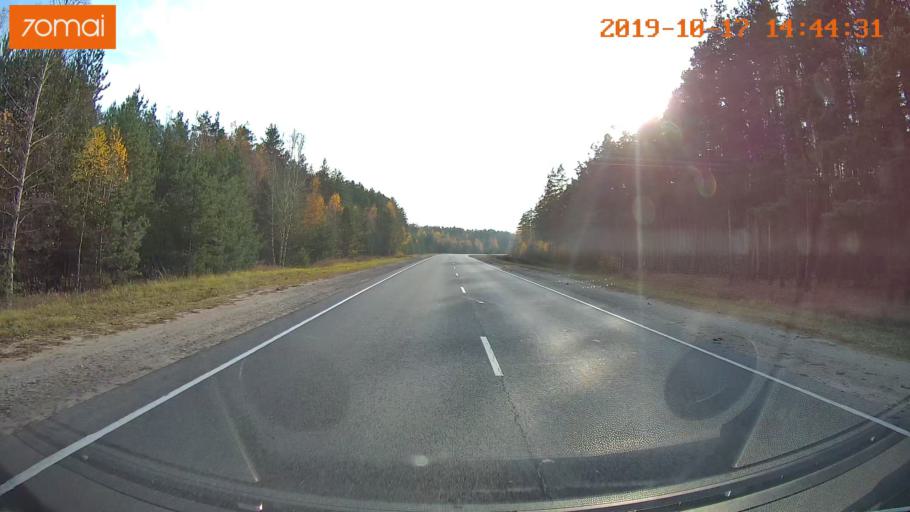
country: RU
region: Rjazan
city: Solotcha
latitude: 54.8117
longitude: 39.8908
